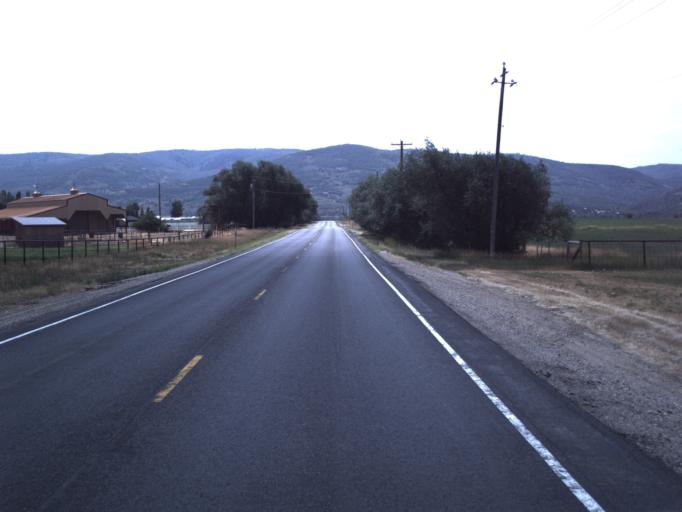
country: US
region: Utah
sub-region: Summit County
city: Francis
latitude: 40.5939
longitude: -111.2423
